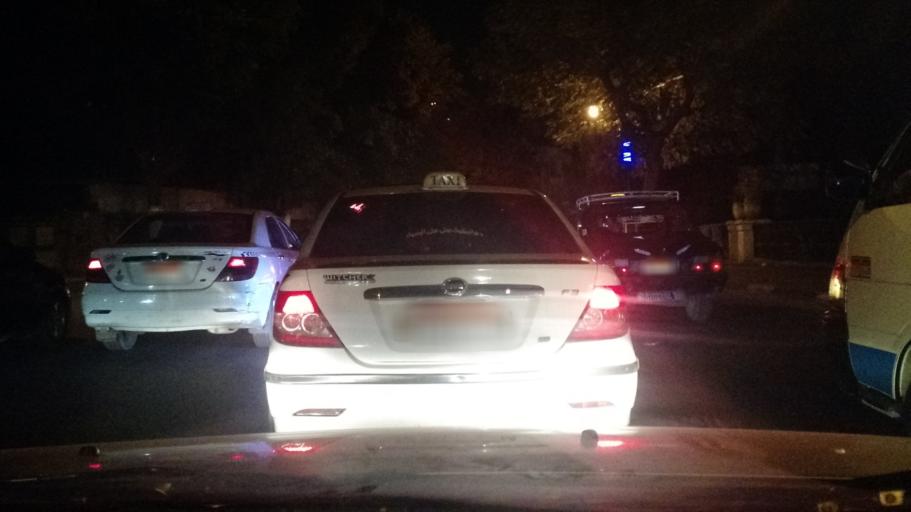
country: EG
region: Al Jizah
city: Al Jizah
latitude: 30.0281
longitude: 31.2312
